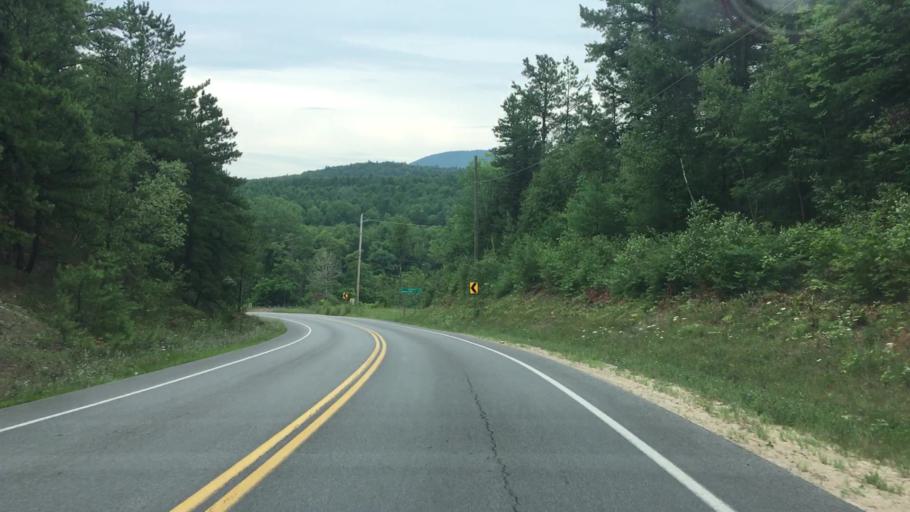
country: US
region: New York
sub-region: Essex County
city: Keeseville
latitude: 44.4659
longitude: -73.5895
